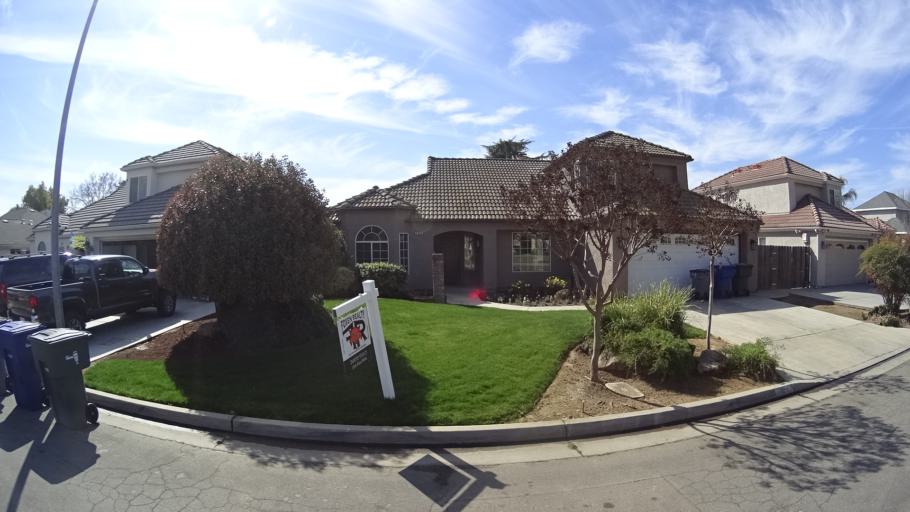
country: US
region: California
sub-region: Fresno County
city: Clovis
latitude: 36.8560
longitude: -119.7595
